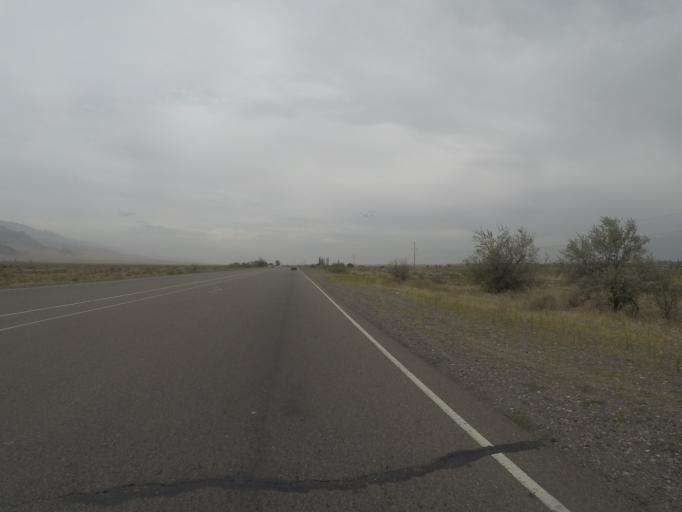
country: KG
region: Chuy
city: Tokmok
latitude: 42.8296
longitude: 75.4701
